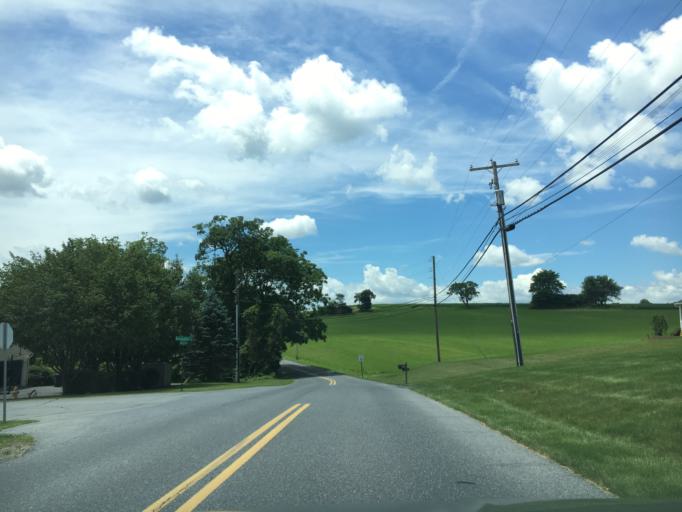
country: US
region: Pennsylvania
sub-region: Lehigh County
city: Laurys Station
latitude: 40.7223
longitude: -75.5373
